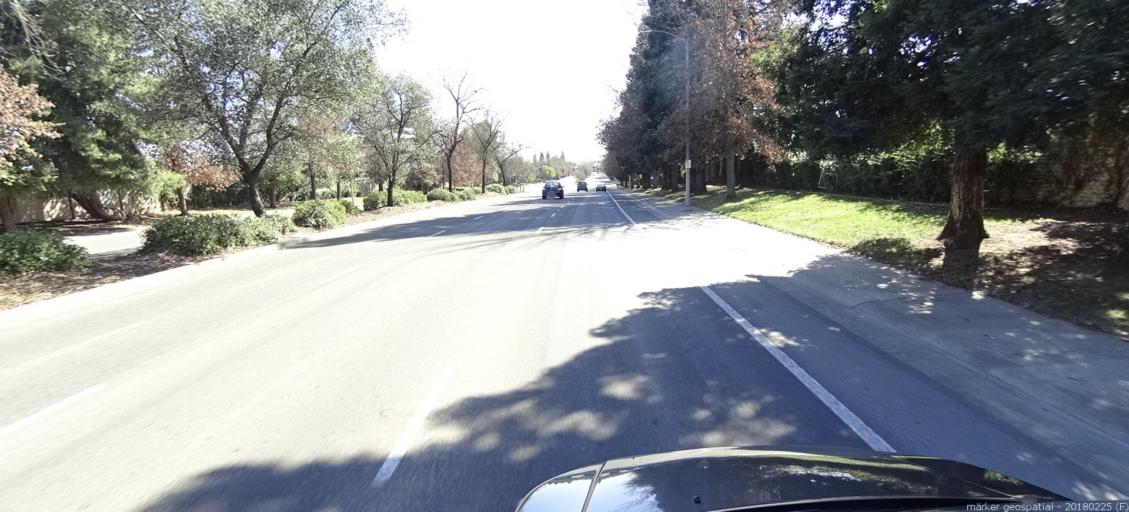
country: US
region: California
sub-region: Sacramento County
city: North Highlands
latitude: 38.7176
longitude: -121.3765
